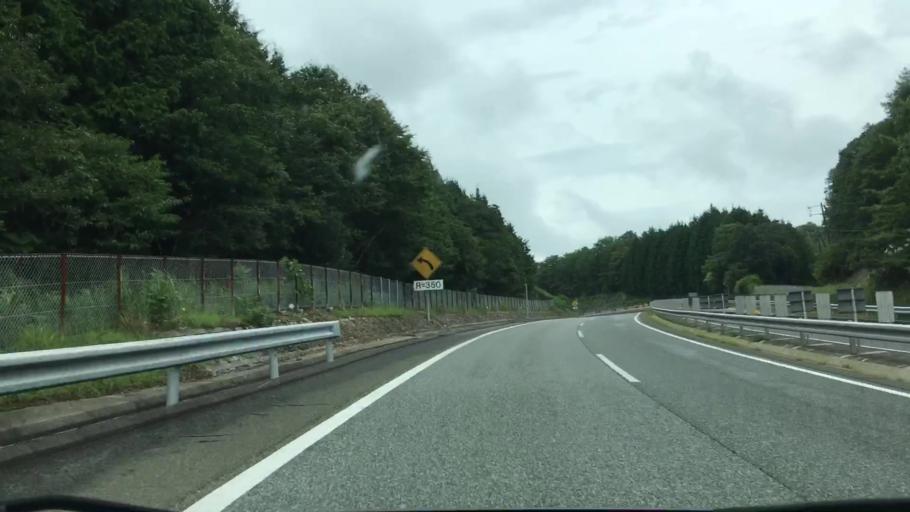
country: JP
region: Hiroshima
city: Shobara
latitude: 34.8721
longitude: 133.1452
